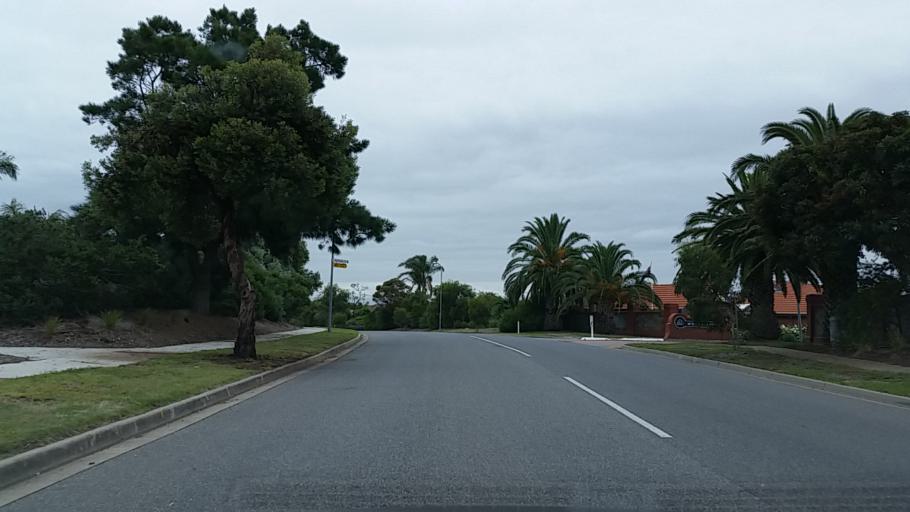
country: AU
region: South Australia
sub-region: Charles Sturt
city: West Lakes Shore
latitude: -34.8619
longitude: 138.4965
